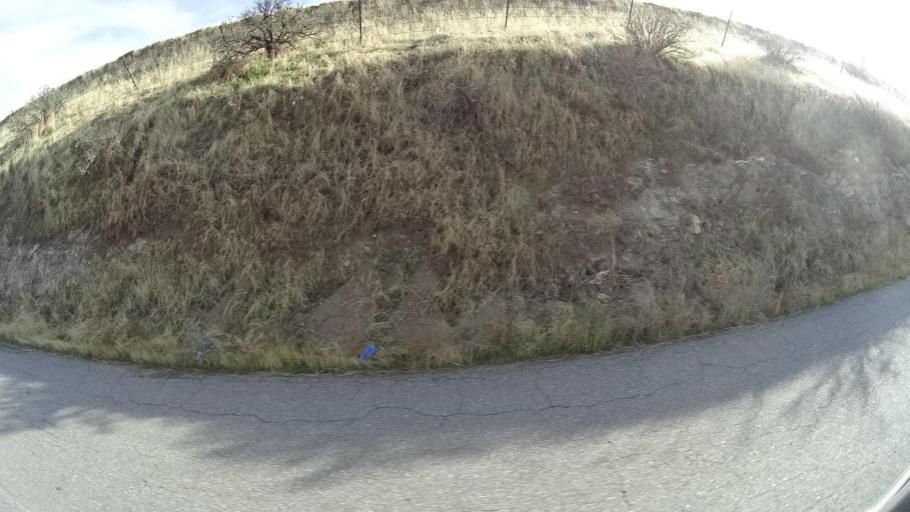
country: US
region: California
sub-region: Kern County
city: Bear Valley Springs
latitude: 35.2816
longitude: -118.6767
